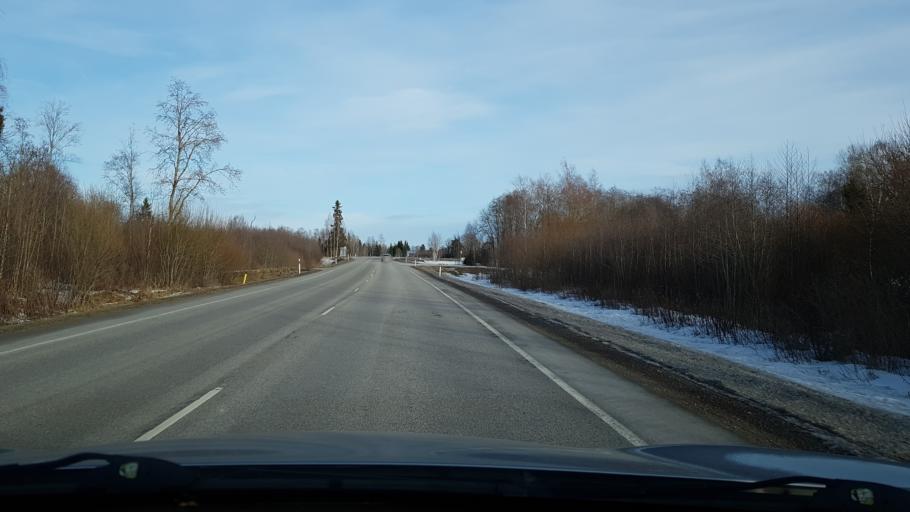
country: EE
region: Viljandimaa
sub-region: Viiratsi vald
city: Viiratsi
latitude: 58.3916
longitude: 25.7988
